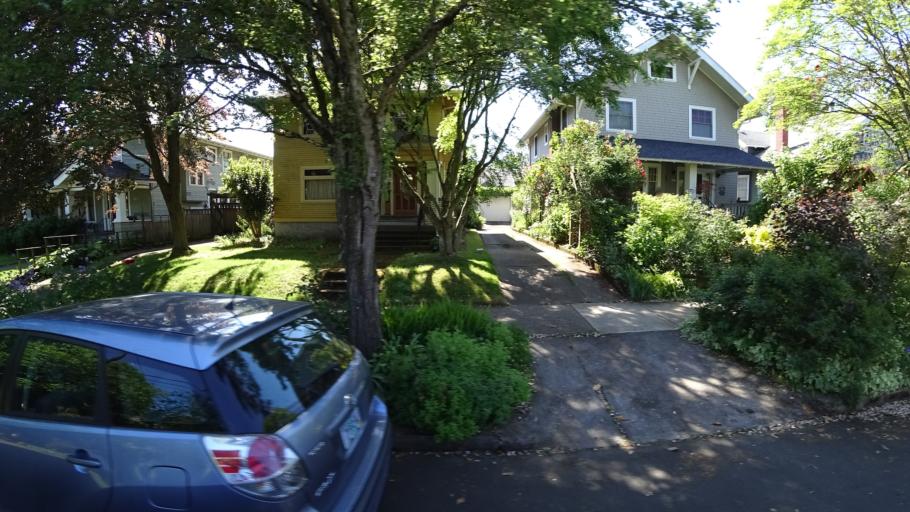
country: US
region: Oregon
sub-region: Multnomah County
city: Portland
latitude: 45.5400
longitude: -122.6566
